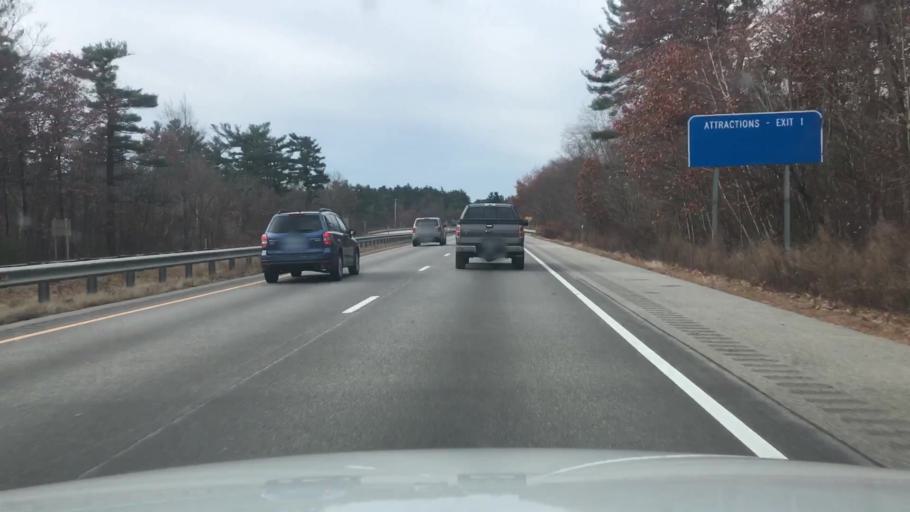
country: US
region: New Hampshire
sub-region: Rockingham County
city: Auburn
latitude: 43.0130
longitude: -71.3812
